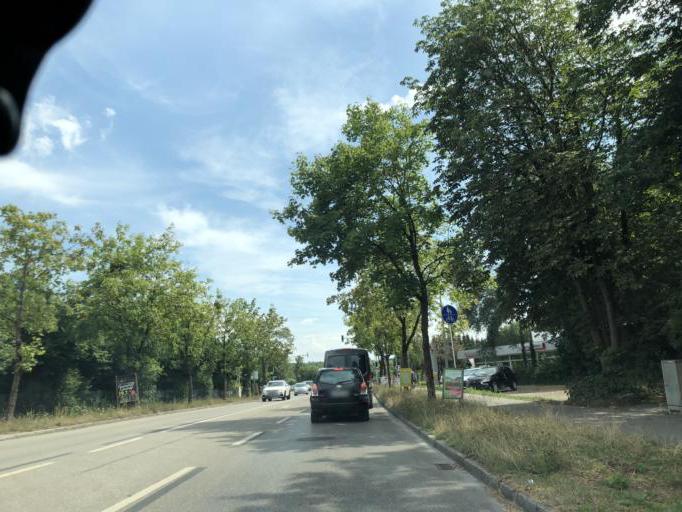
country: DE
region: Bavaria
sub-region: Upper Bavaria
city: Grobenzell
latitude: 48.1834
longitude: 11.3881
